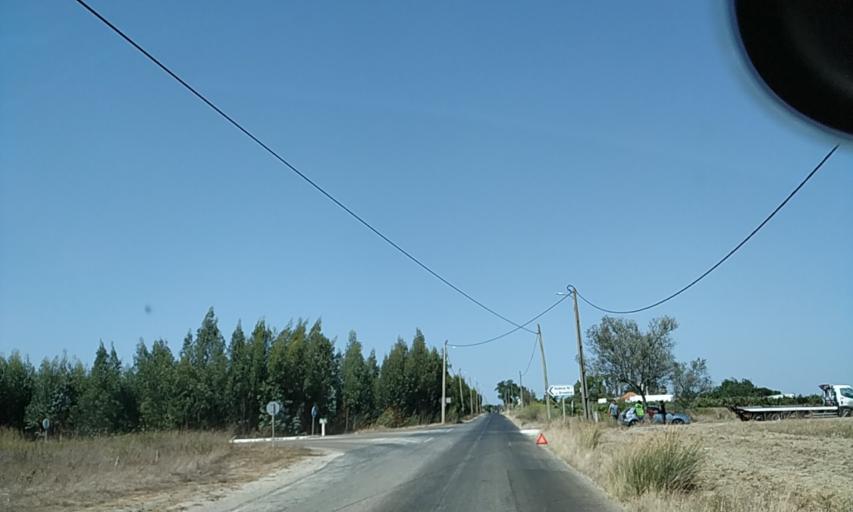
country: PT
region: Santarem
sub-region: Benavente
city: Poceirao
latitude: 38.7135
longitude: -8.7147
